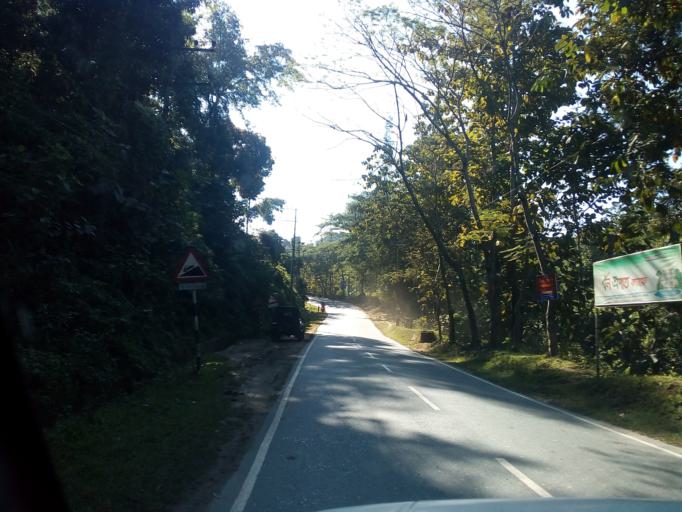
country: BD
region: Chittagong
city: Bandarban
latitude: 22.1844
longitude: 92.2079
